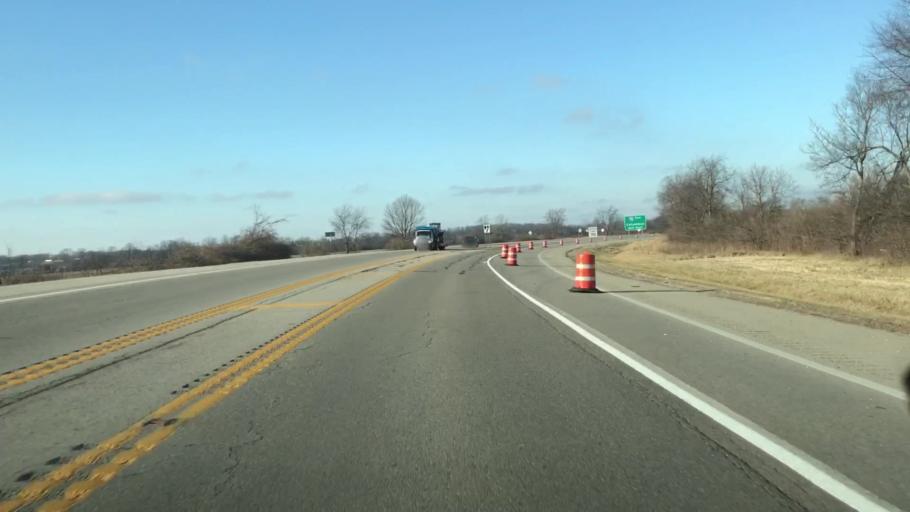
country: US
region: Ohio
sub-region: Clark County
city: Springfield
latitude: 39.8833
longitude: -83.8532
